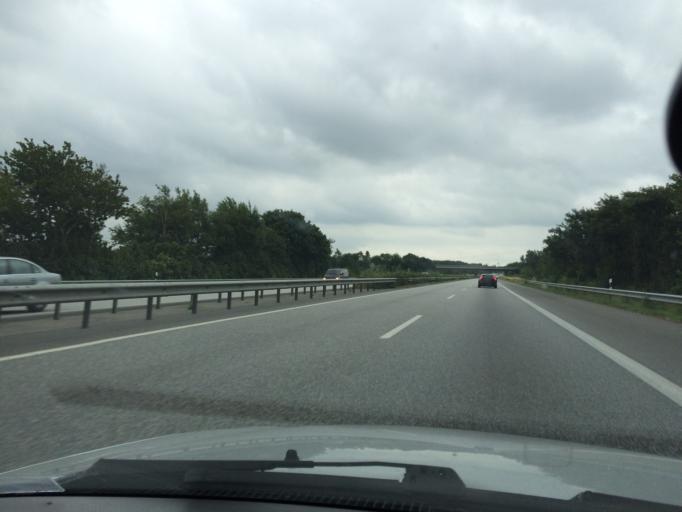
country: DE
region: Schleswig-Holstein
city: Tarp
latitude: 54.6817
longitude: 9.4179
